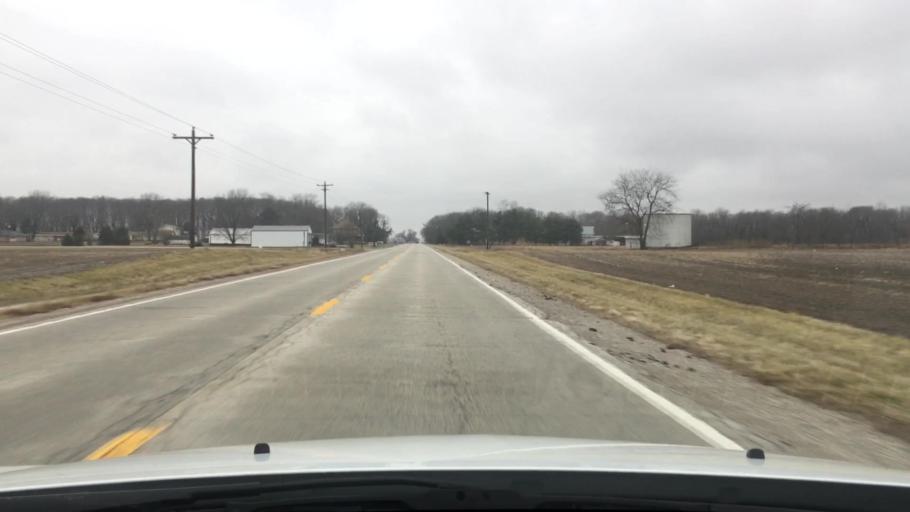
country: US
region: Illinois
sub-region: Iroquois County
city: Clifton
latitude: 40.8879
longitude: -87.8259
